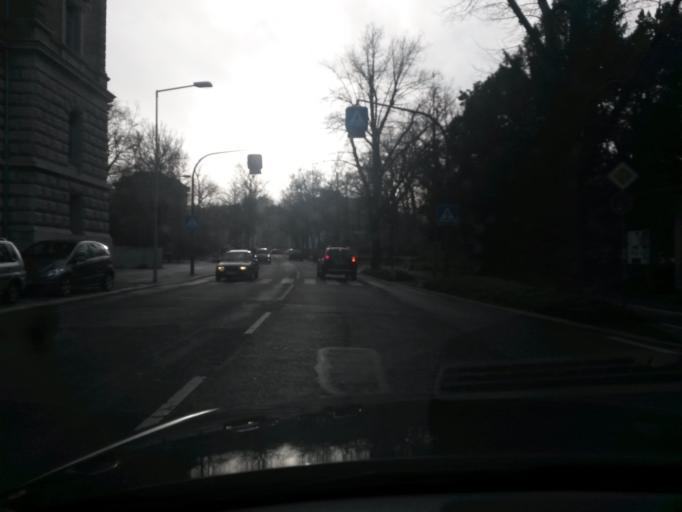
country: DE
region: Bavaria
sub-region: Regierungsbezirk Unterfranken
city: Wuerzburg
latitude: 49.7888
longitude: 9.9365
